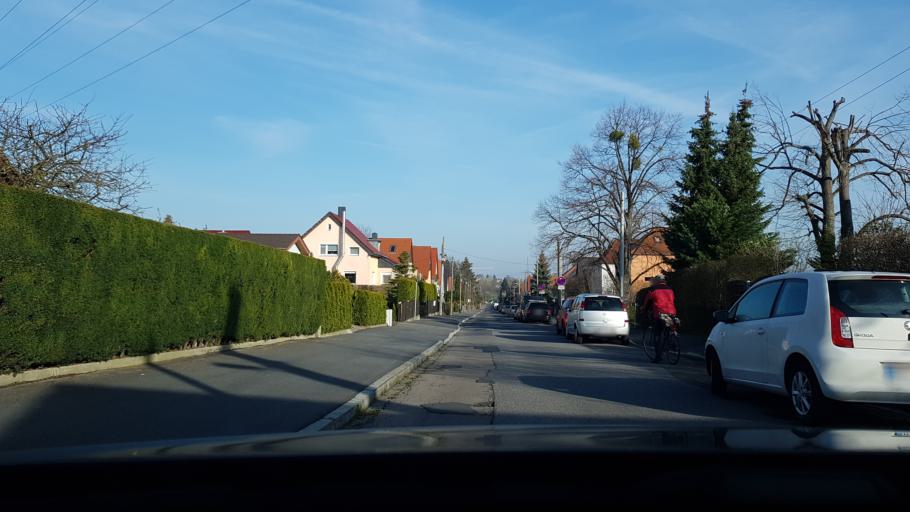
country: DE
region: Saxony
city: Kreischa
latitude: 50.9979
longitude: 13.7872
